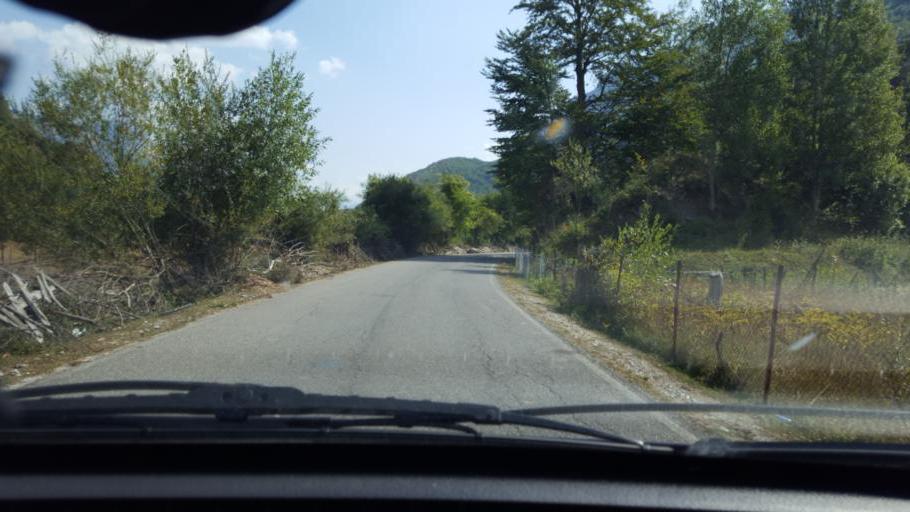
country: ME
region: Andrijevica
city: Andrijevica
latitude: 42.5829
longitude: 19.7336
